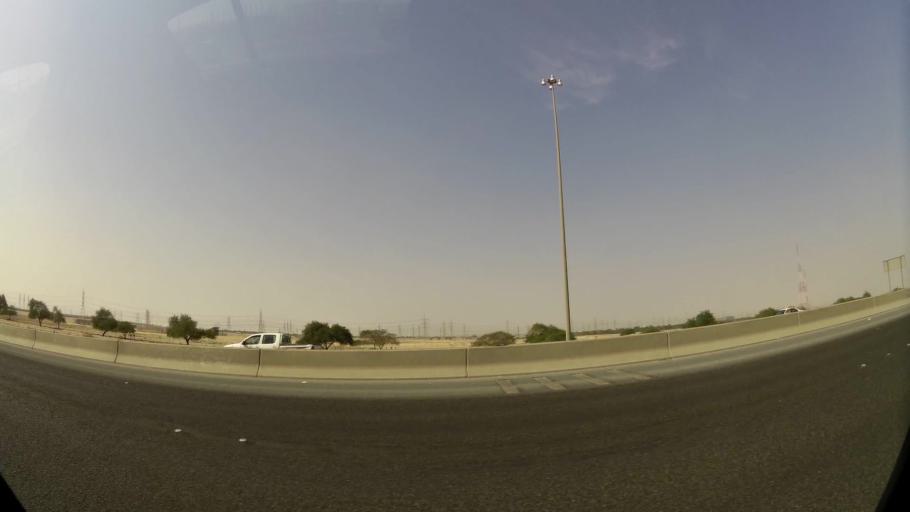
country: KW
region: Al Ahmadi
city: Al Fahahil
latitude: 29.0700
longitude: 48.1110
